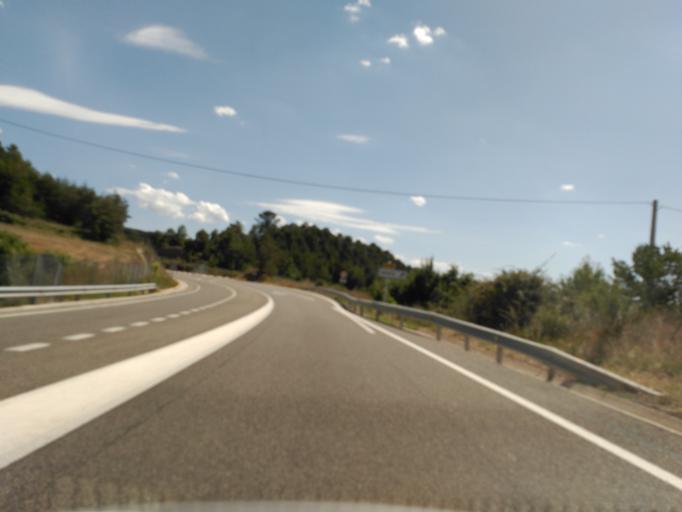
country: ES
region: Catalonia
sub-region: Provincia de Barcelona
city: Olost
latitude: 41.9638
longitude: 2.1288
